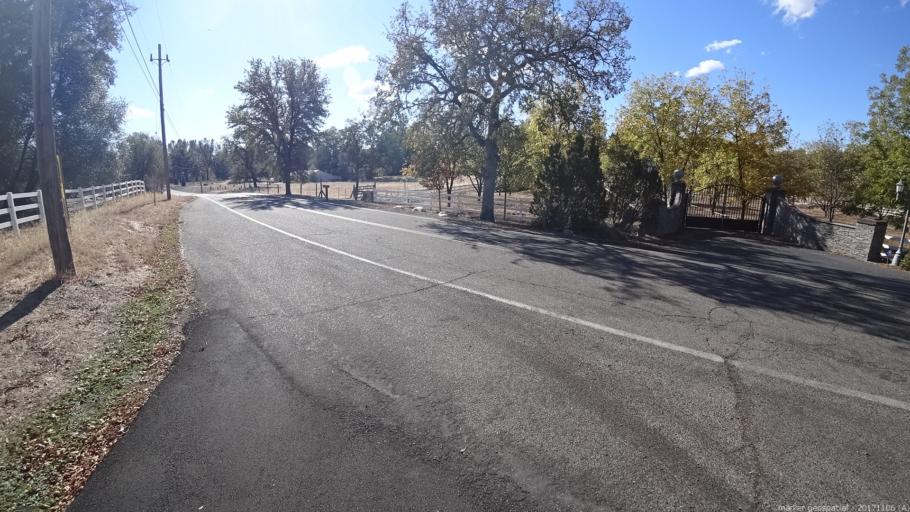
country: US
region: California
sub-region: Shasta County
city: Palo Cedro
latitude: 40.5883
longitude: -122.2238
